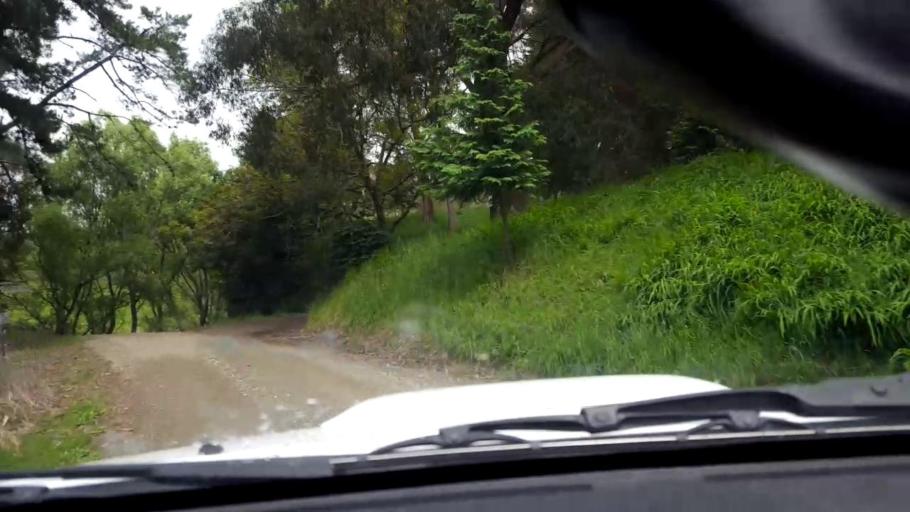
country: NZ
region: Gisborne
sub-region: Gisborne District
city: Gisborne
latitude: -38.3847
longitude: 177.6308
